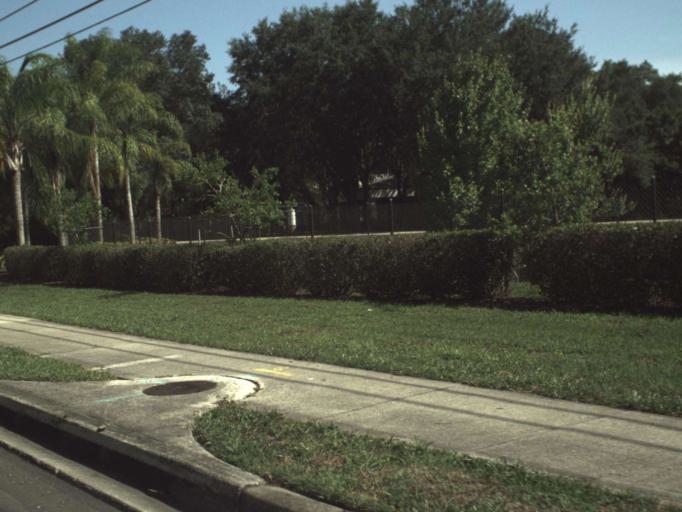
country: US
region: Florida
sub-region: Seminole County
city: Winter Springs
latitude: 28.7033
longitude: -81.2688
